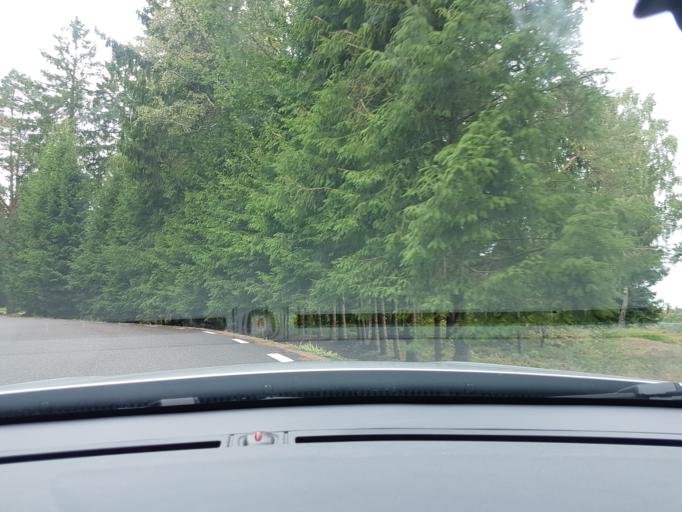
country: SE
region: Vaestra Goetaland
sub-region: Ale Kommun
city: Alvangen
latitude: 57.9094
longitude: 12.1612
